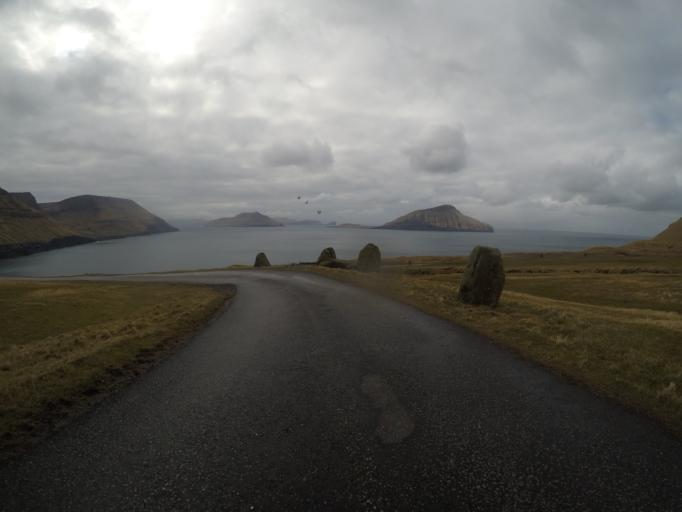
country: FO
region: Streymoy
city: Kollafjordhur
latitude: 62.0410
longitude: -6.9554
